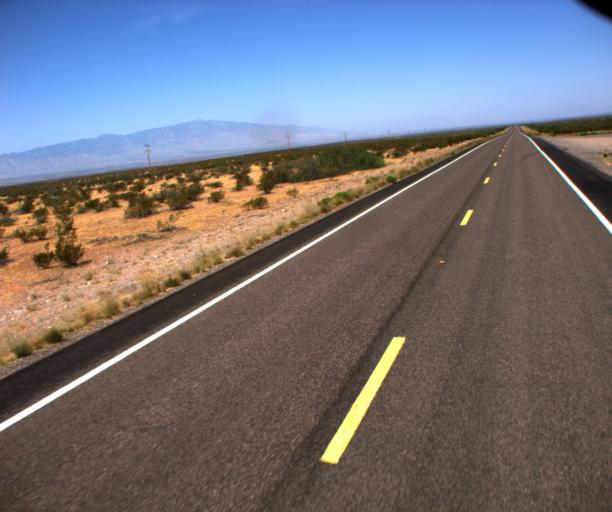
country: US
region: Arizona
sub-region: Graham County
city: Swift Trail Junction
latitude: 32.7604
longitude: -109.4392
